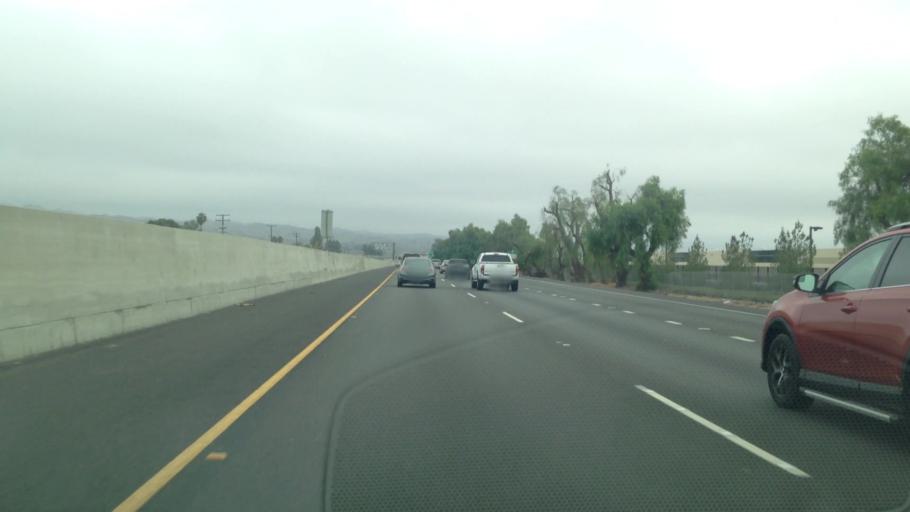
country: US
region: California
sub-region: Riverside County
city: Moreno Valley
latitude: 33.9393
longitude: -117.1656
